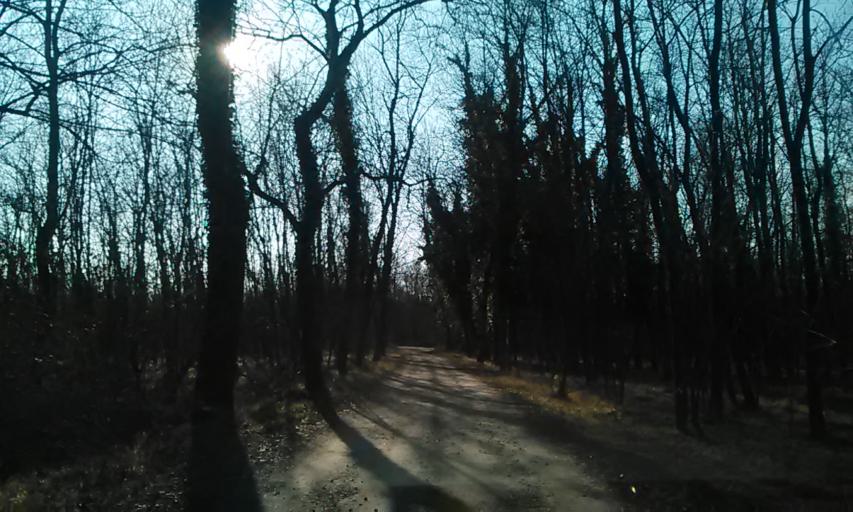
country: IT
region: Piedmont
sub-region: Provincia di Vercelli
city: Lenta
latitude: 45.5849
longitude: 8.3789
